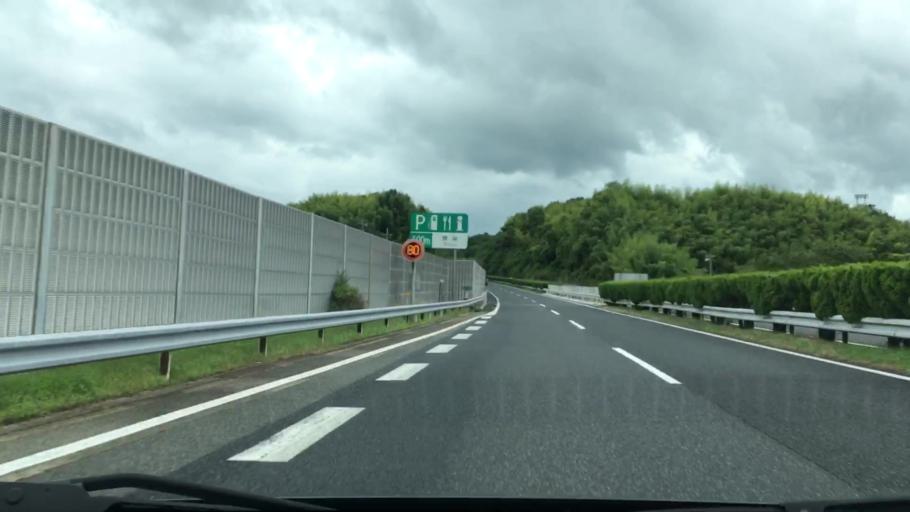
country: JP
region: Okayama
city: Tsuyama
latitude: 35.0442
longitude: 134.1156
